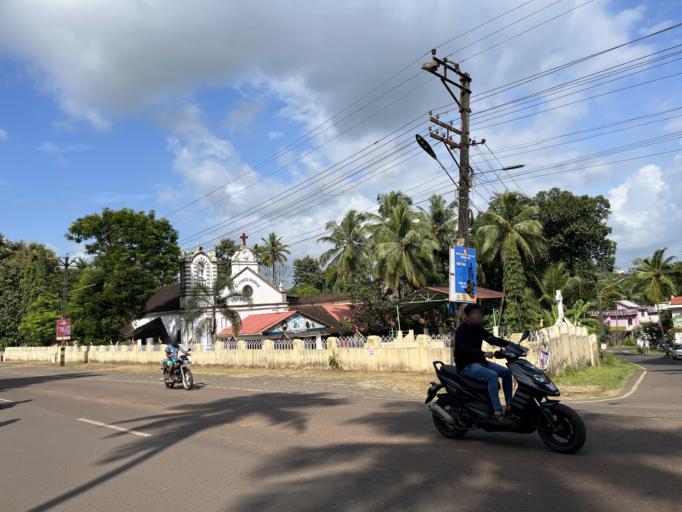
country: IN
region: Goa
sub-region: North Goa
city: Ponda
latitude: 15.4026
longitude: 74.0145
